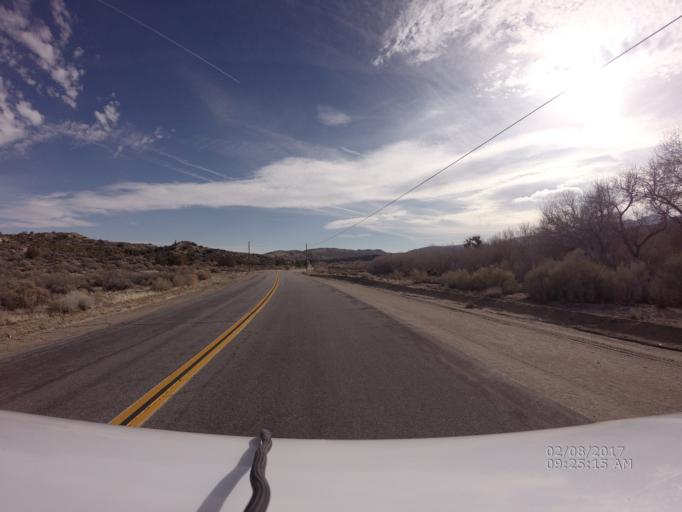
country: US
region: California
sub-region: Los Angeles County
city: Littlerock
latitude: 34.4559
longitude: -117.8827
